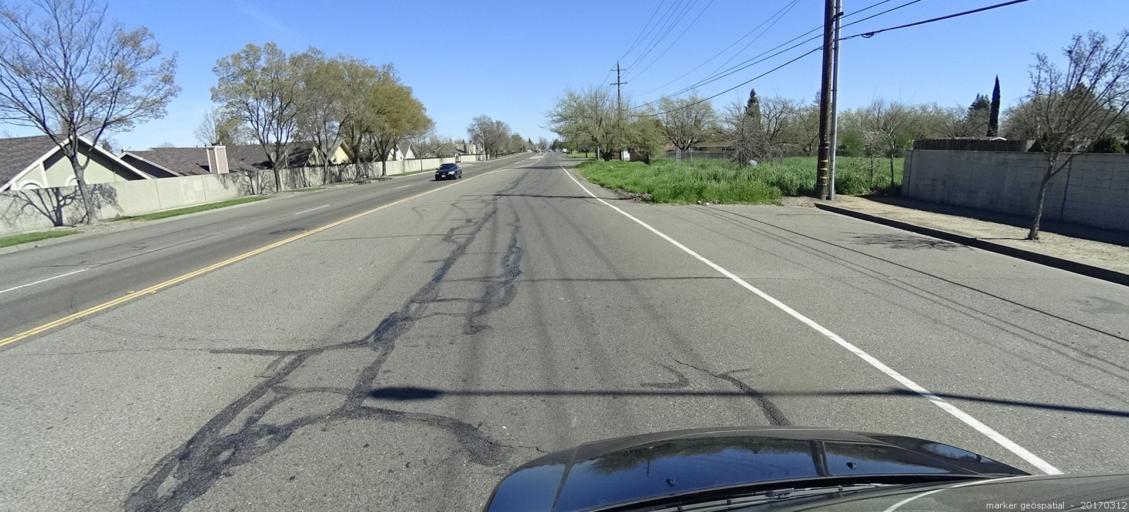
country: US
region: California
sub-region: Sacramento County
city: Rio Linda
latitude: 38.6550
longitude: -121.4643
